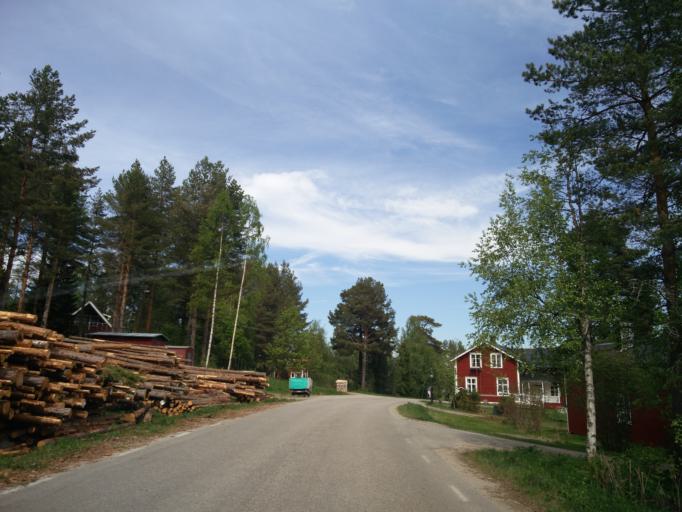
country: SE
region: Gaevleborg
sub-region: Hudiksvalls Kommun
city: Sorforsa
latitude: 61.6921
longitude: 16.9235
